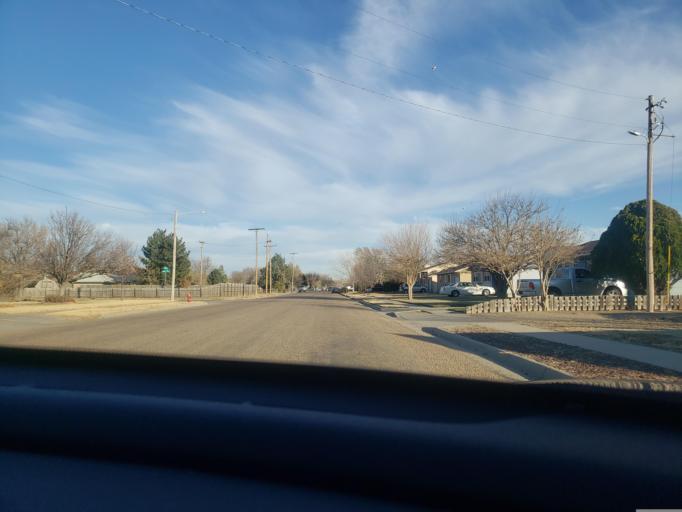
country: US
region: Kansas
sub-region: Finney County
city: Garden City
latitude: 37.9859
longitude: -100.8771
